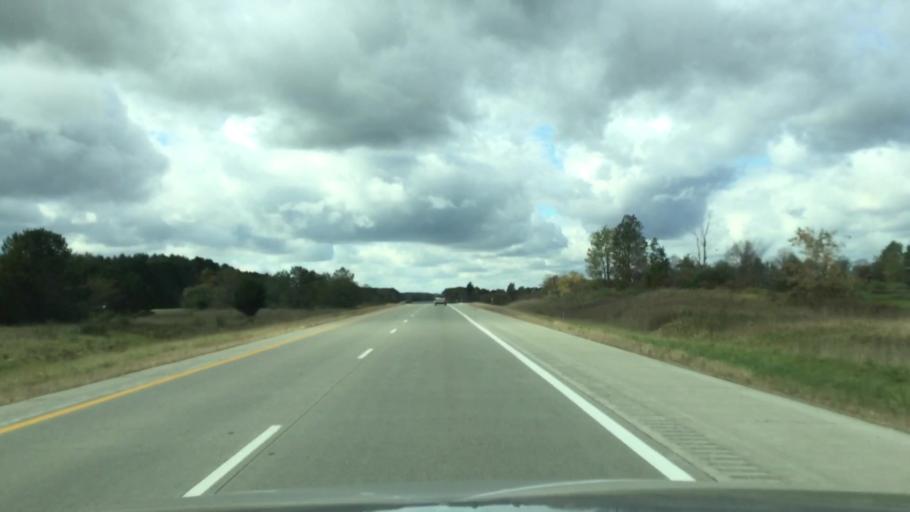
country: US
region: Michigan
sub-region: Lapeer County
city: Lapeer
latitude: 43.0260
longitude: -83.3965
